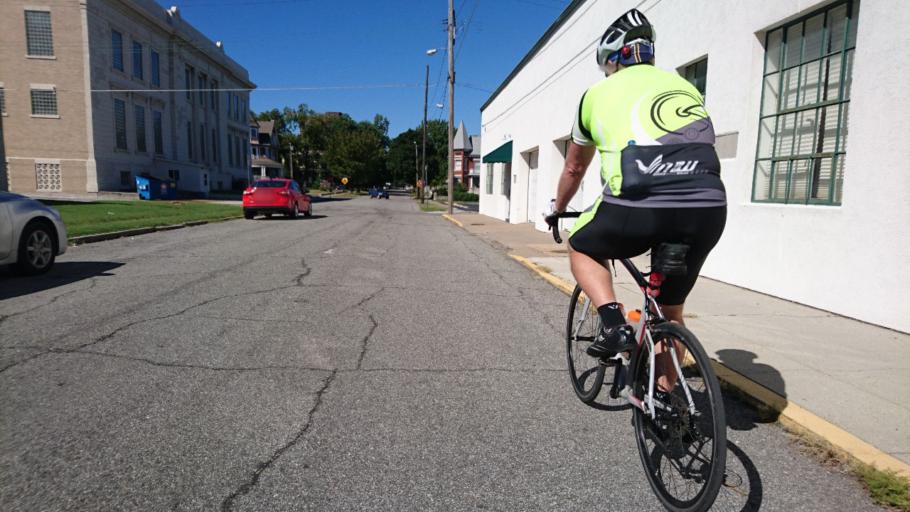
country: US
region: Missouri
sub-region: Jasper County
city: Joplin
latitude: 37.0869
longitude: -94.5169
